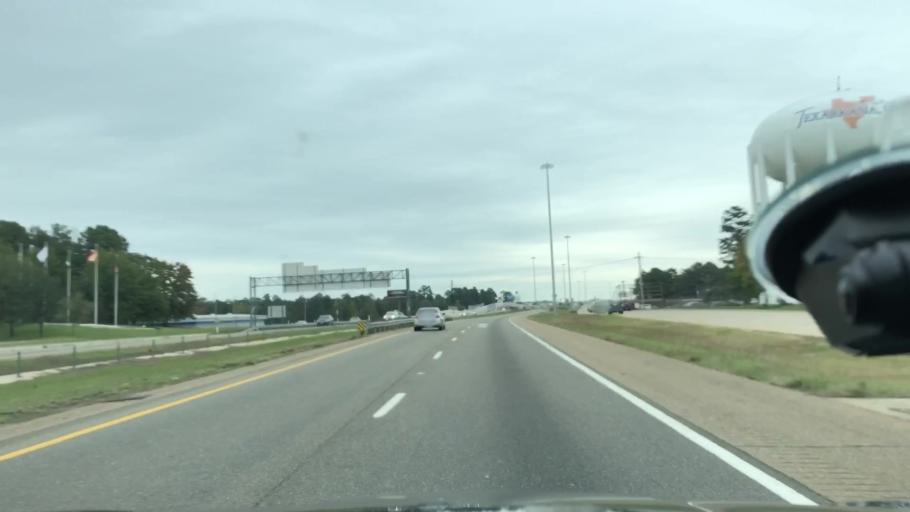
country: US
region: Arkansas
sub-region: Miller County
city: Texarkana
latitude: 33.4693
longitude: -94.0559
